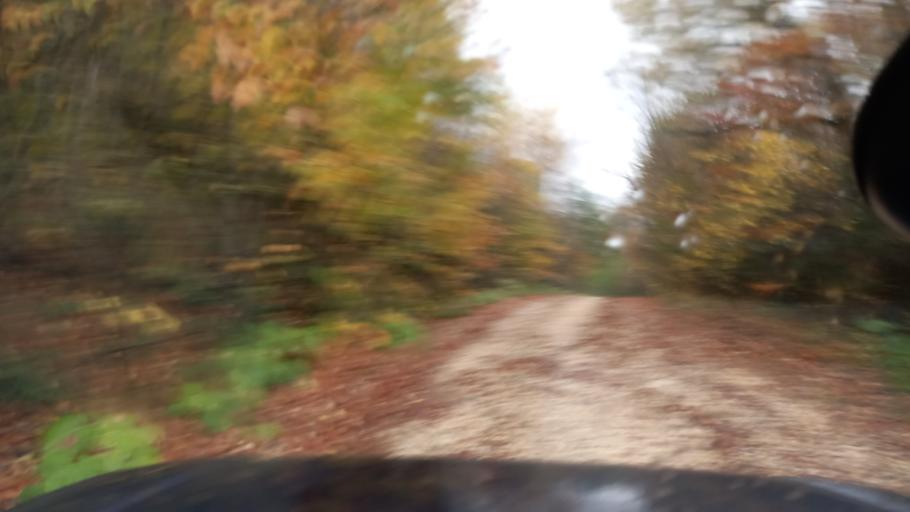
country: RU
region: Krasnodarskiy
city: Neftegorsk
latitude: 44.0261
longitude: 39.8409
